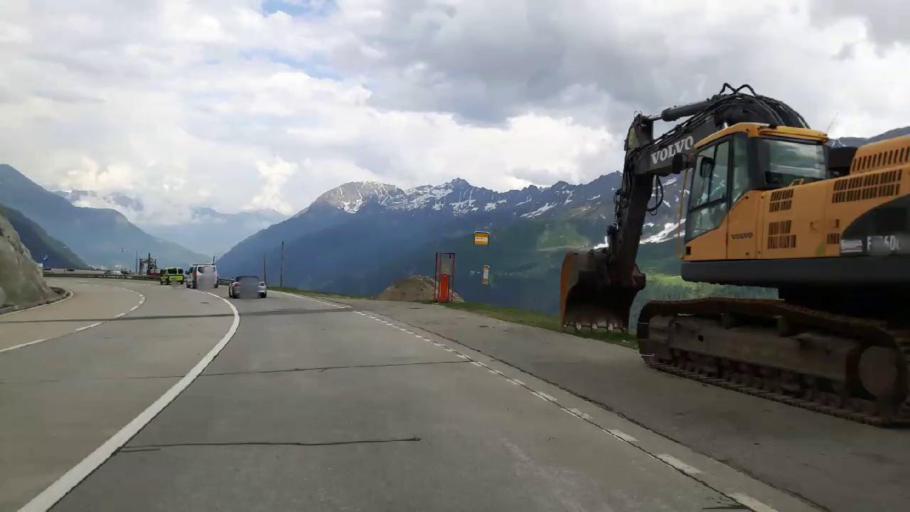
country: CH
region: Ticino
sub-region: Leventina District
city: Airolo
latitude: 46.5363
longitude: 8.5684
